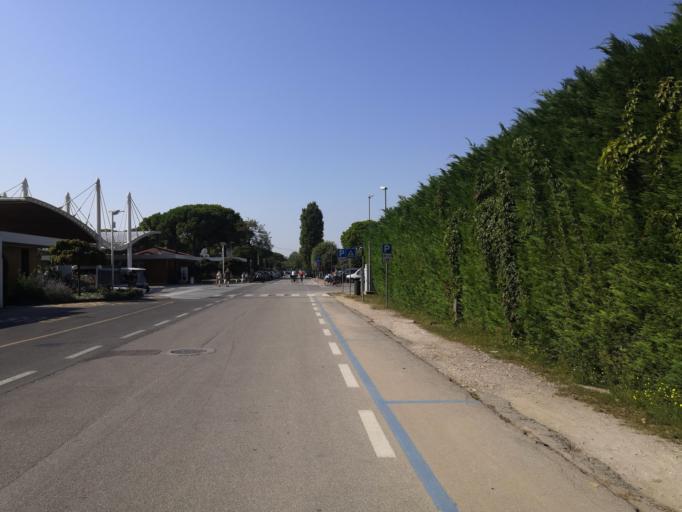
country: IT
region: Veneto
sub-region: Provincia di Venezia
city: Ca' Savio
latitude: 45.4379
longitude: 12.4385
